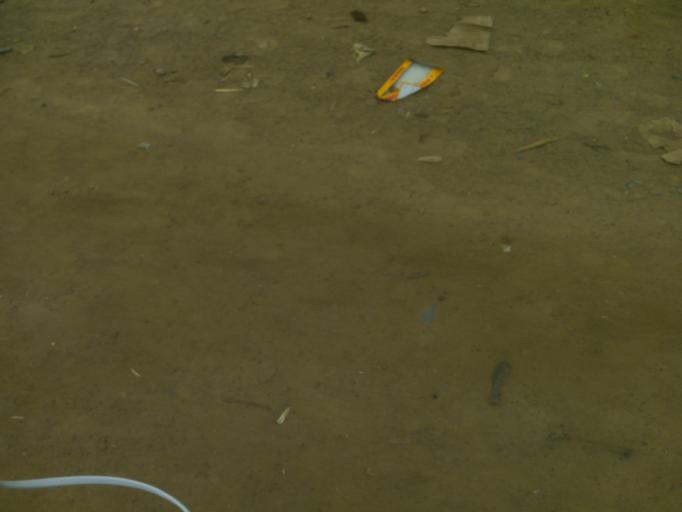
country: ML
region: Kayes
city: Yelimane
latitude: 14.6445
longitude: -10.6989
